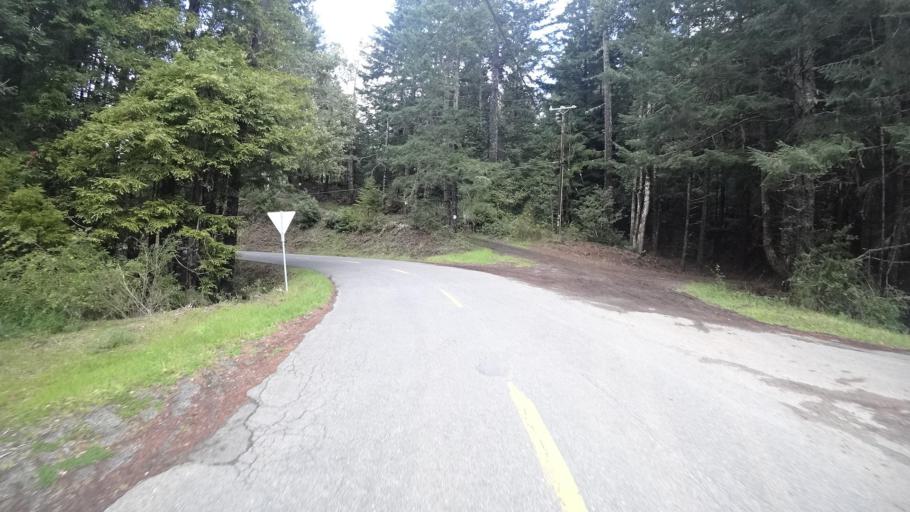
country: US
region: California
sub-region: Humboldt County
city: Bayside
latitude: 40.7486
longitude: -123.9719
